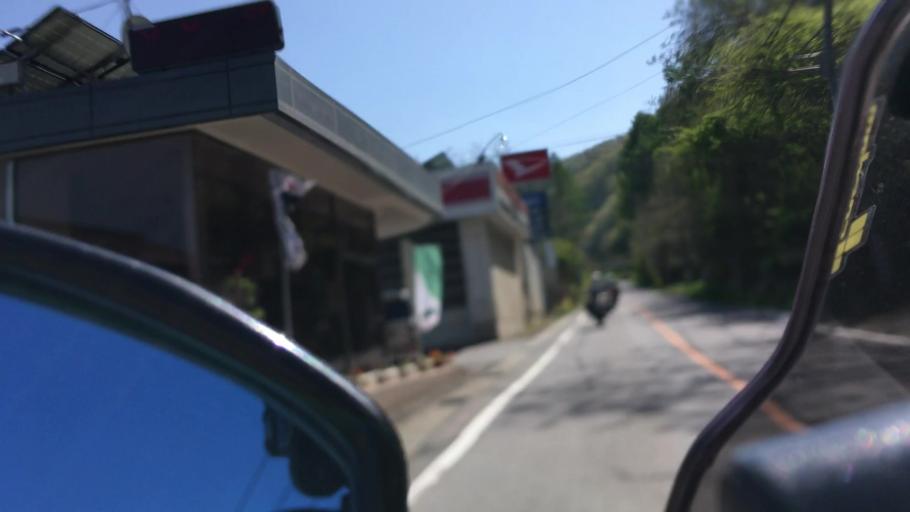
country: JP
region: Nagano
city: Komoro
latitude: 36.4924
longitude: 138.4908
